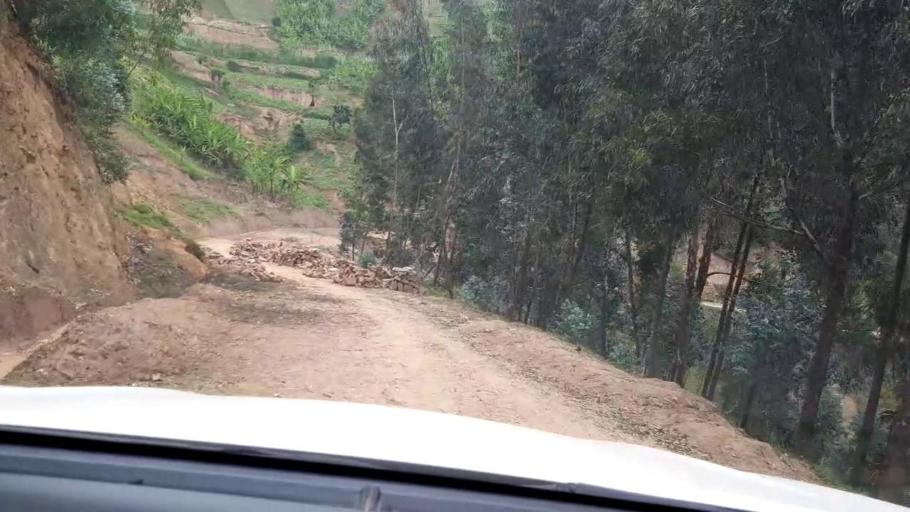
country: RW
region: Western Province
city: Kibuye
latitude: -1.8272
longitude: 29.5457
